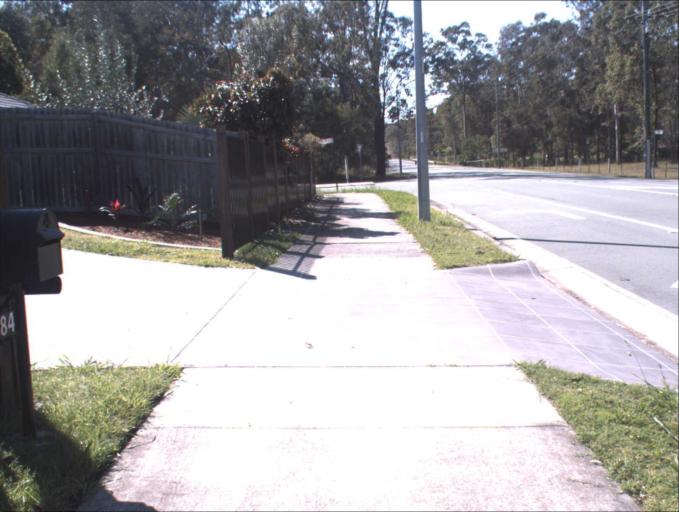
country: AU
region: Queensland
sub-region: Logan
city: Waterford West
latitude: -27.7183
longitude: 153.1443
